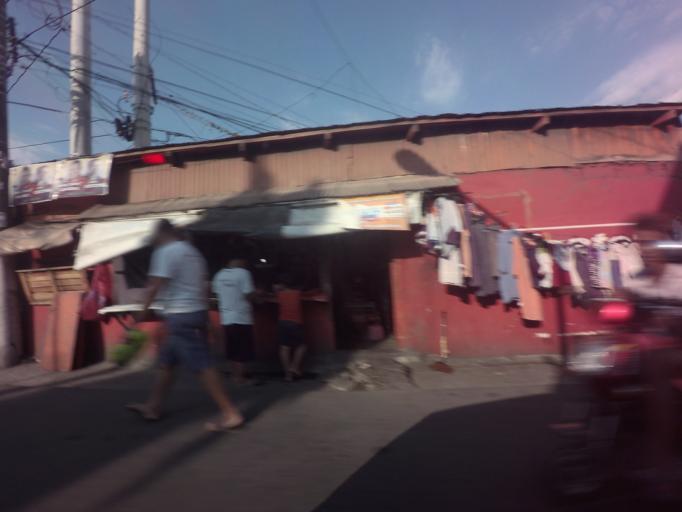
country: PH
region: Calabarzon
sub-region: Province of Rizal
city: Taguig
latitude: 14.4791
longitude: 121.0599
